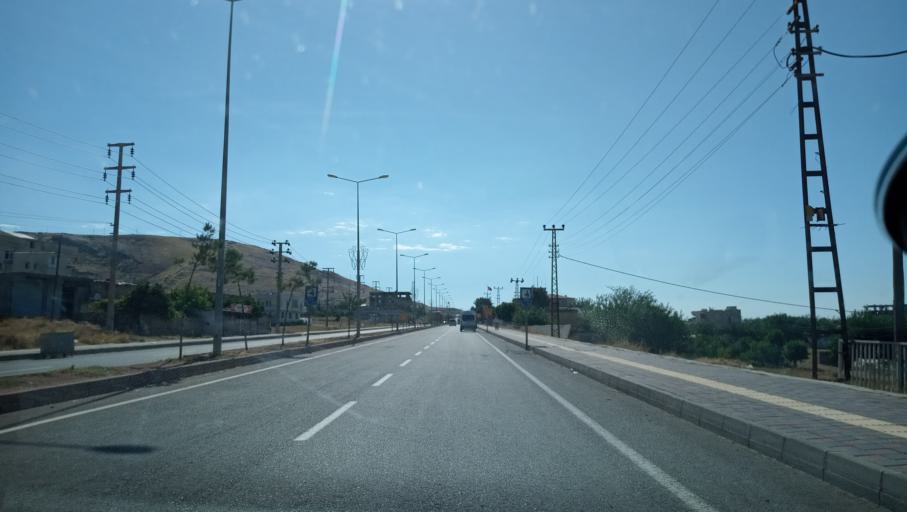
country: TR
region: Diyarbakir
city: Silvan
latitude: 38.1358
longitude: 41.0267
